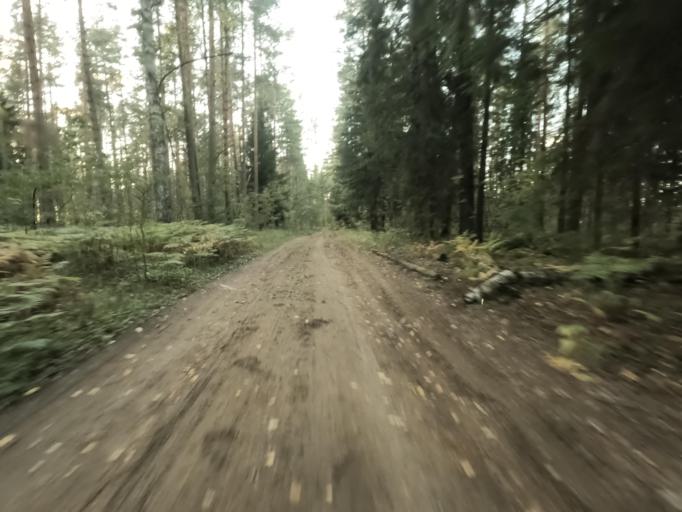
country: RU
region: Leningrad
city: Otradnoye
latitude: 59.8371
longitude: 30.8062
